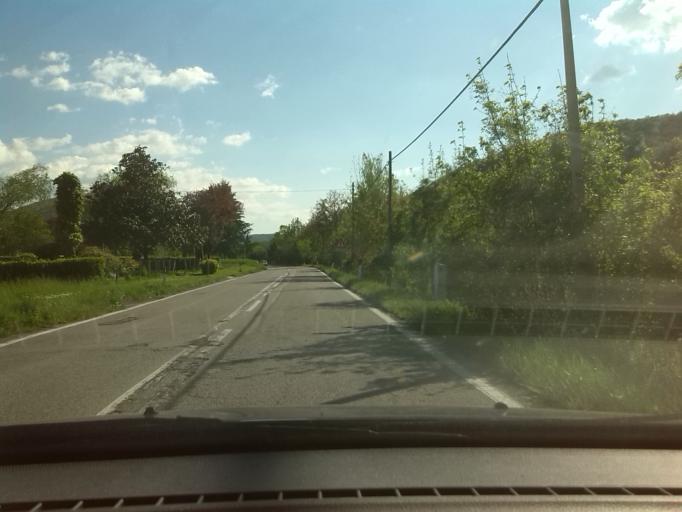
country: IT
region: Friuli Venezia Giulia
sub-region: Provincia di Udine
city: San Pietro al Natisone
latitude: 46.1377
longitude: 13.4860
